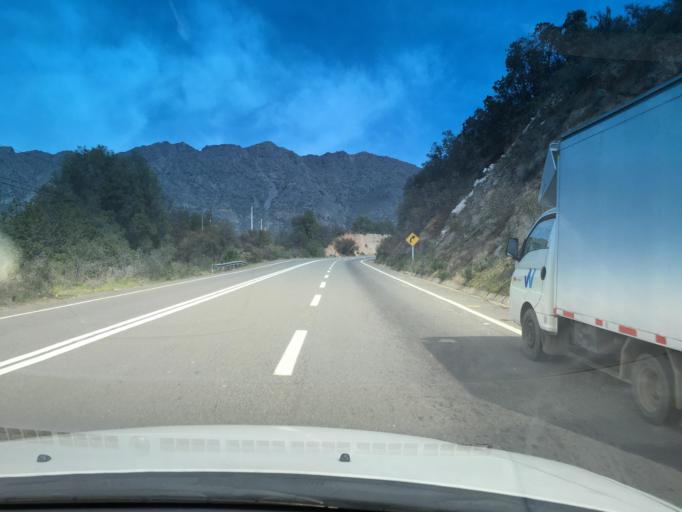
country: CL
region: Valparaiso
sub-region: Provincia de San Felipe
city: Llaillay
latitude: -33.0688
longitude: -70.9952
